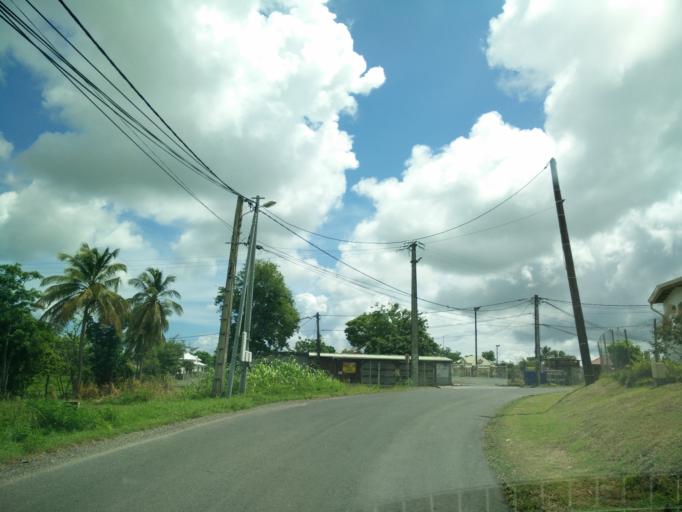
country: GP
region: Guadeloupe
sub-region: Guadeloupe
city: Le Moule
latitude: 16.2745
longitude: -61.3374
